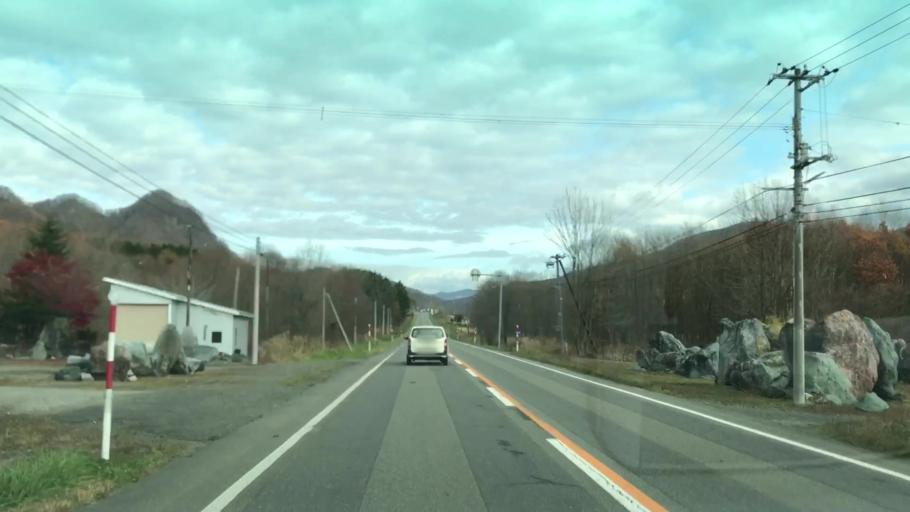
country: JP
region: Hokkaido
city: Shizunai-furukawacho
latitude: 42.7732
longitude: 142.3830
